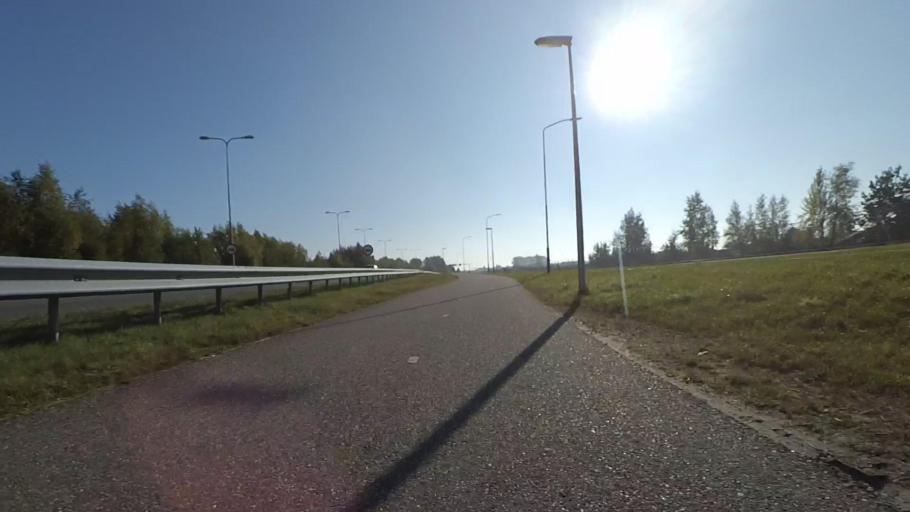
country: NL
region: Gelderland
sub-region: Gemeente Harderwijk
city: Harderwijk
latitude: 52.3592
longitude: 5.6222
